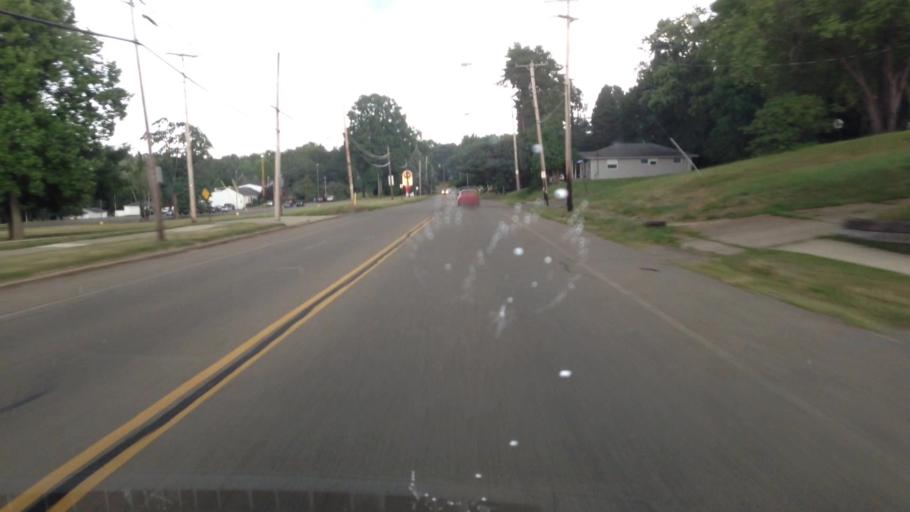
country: US
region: Ohio
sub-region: Summit County
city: Barberton
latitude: 41.0211
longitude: -81.5821
